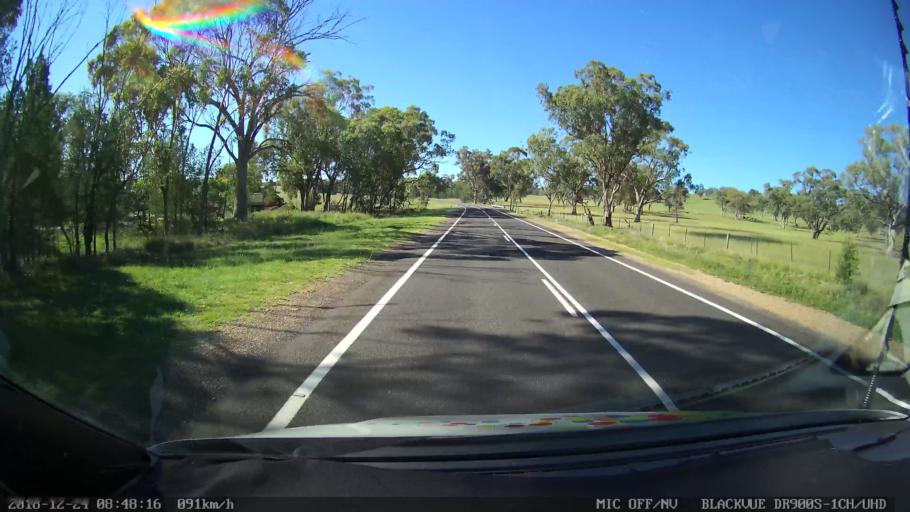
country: AU
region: New South Wales
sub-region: Liverpool Plains
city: Quirindi
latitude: -31.4534
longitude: 150.6459
